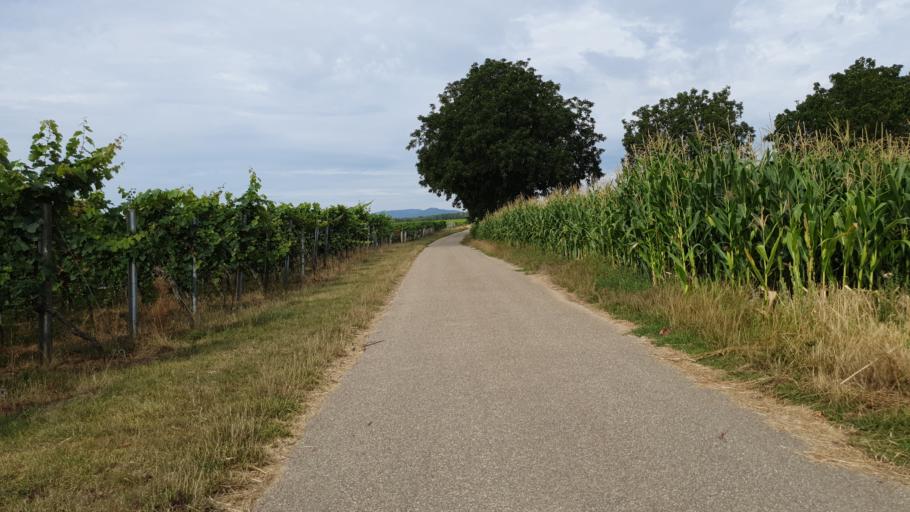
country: DE
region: Rheinland-Pfalz
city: Hergersweiler
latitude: 49.1138
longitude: 8.0965
